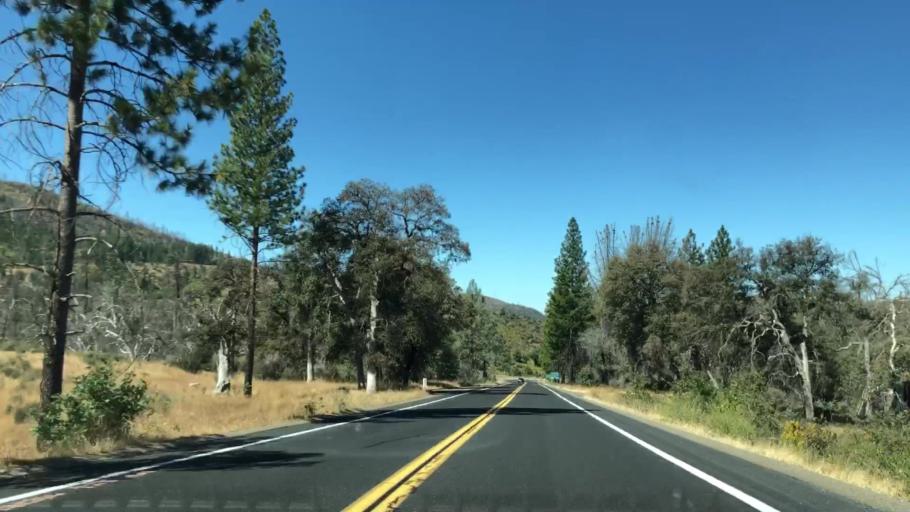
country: US
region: California
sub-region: Tuolumne County
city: Tuolumne City
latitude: 37.8246
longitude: -120.0069
